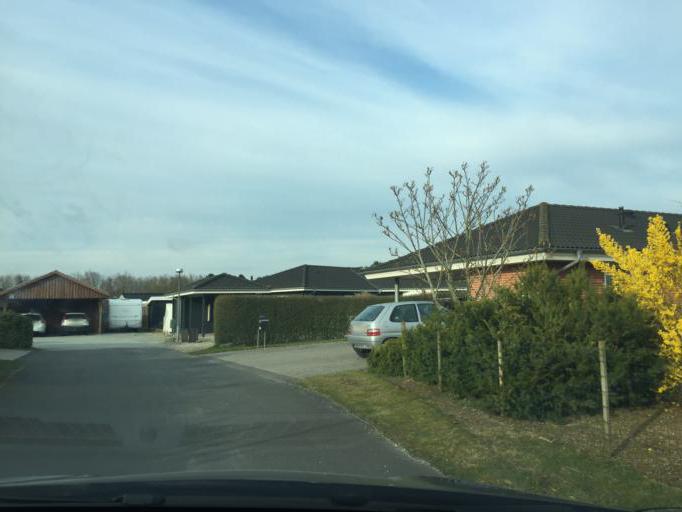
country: DK
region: South Denmark
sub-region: Kerteminde Kommune
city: Langeskov
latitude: 55.3223
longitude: 10.5720
